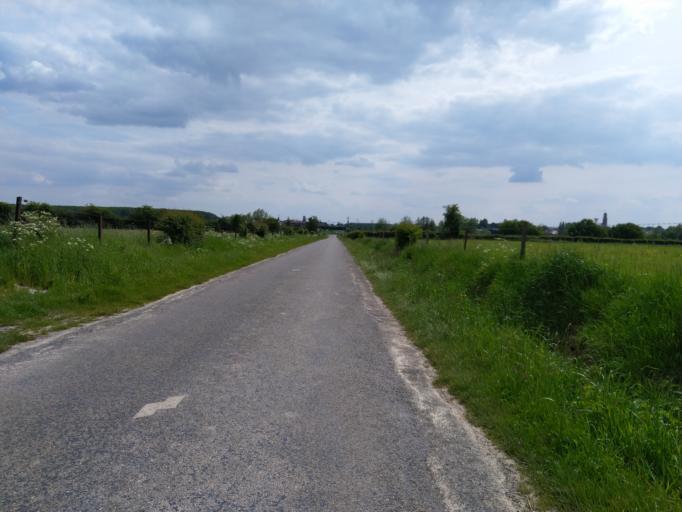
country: FR
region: Picardie
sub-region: Departement de l'Aisne
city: Boue
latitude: 50.0285
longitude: 3.6790
